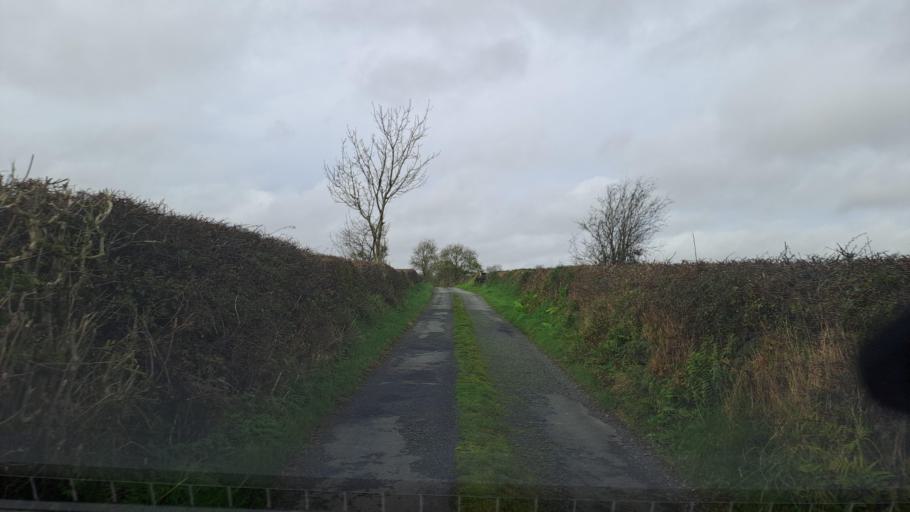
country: IE
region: Ulster
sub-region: County Monaghan
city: Carrickmacross
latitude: 54.0107
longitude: -6.7981
